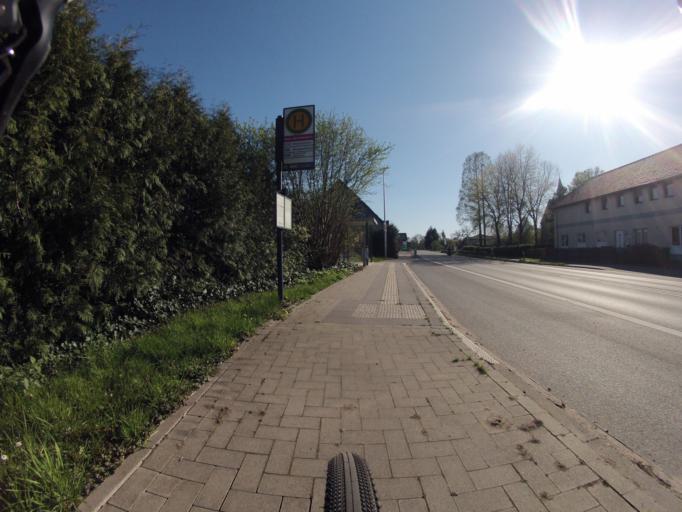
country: DE
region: North Rhine-Westphalia
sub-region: Regierungsbezirk Munster
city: Birgte
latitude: 52.2315
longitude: 7.6902
